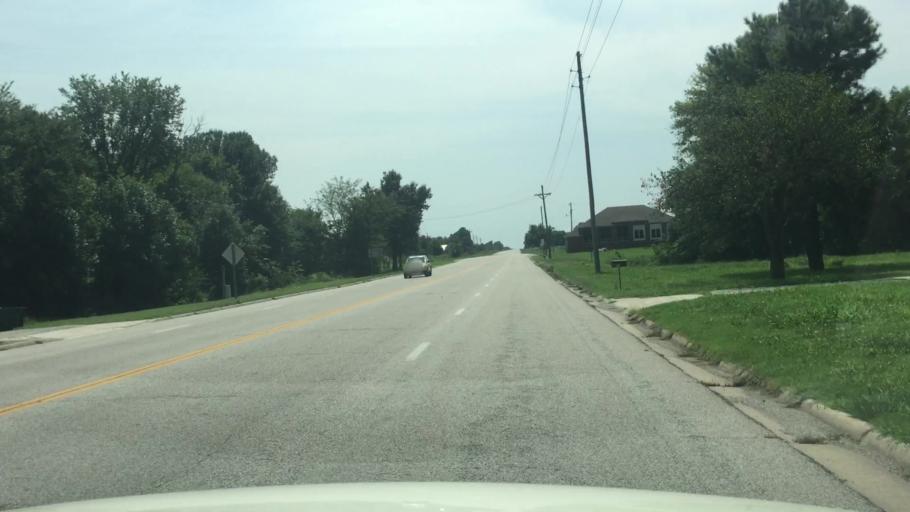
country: US
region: Kansas
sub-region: Cherokee County
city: Galena
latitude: 37.1649
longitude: -94.7044
